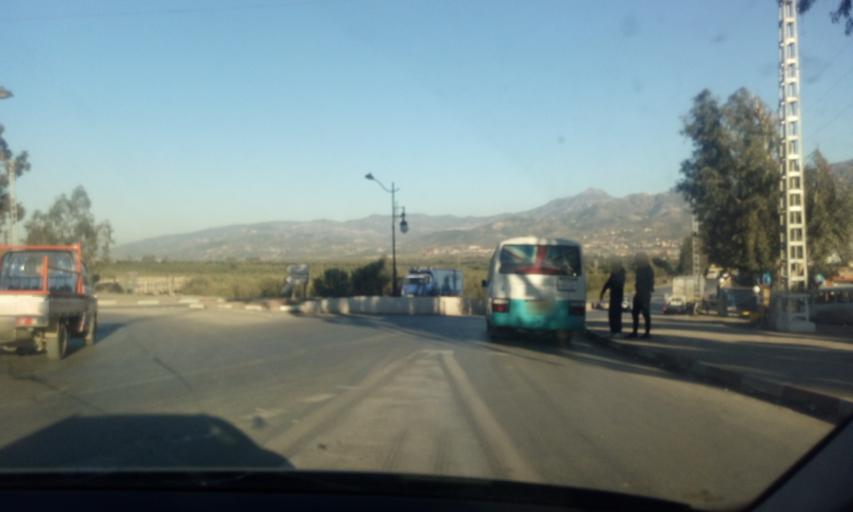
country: DZ
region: Bejaia
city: Akbou
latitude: 36.4833
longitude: 4.5589
